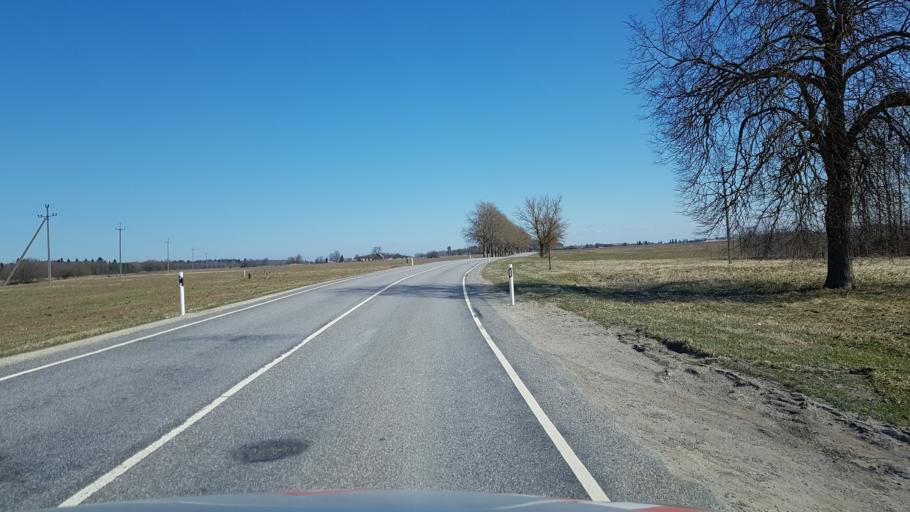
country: EE
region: Ida-Virumaa
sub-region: Johvi vald
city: Johvi
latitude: 59.3374
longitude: 27.3366
